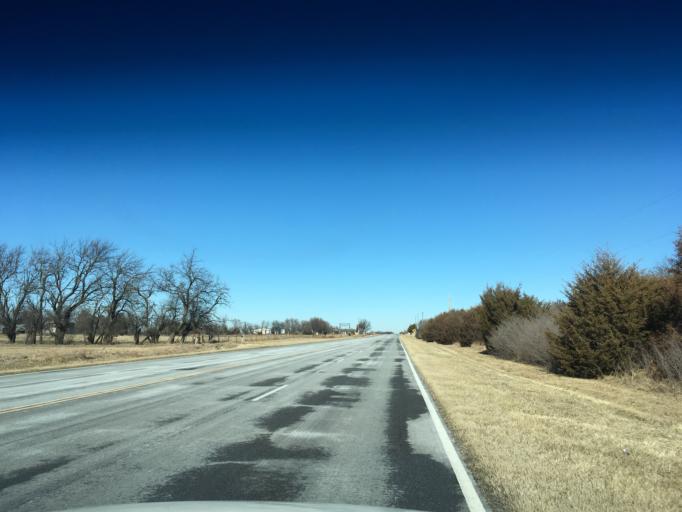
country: US
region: Kansas
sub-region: Harvey County
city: Sedgwick
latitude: 37.9522
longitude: -97.3364
